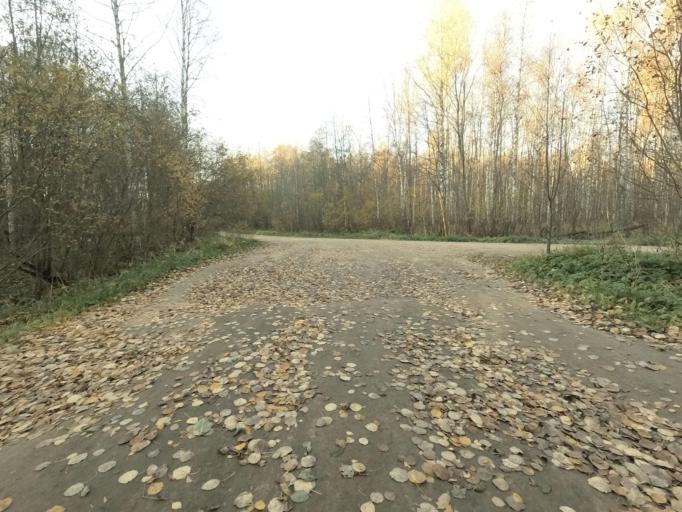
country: RU
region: Leningrad
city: Sinyavino
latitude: 59.8779
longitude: 31.0397
